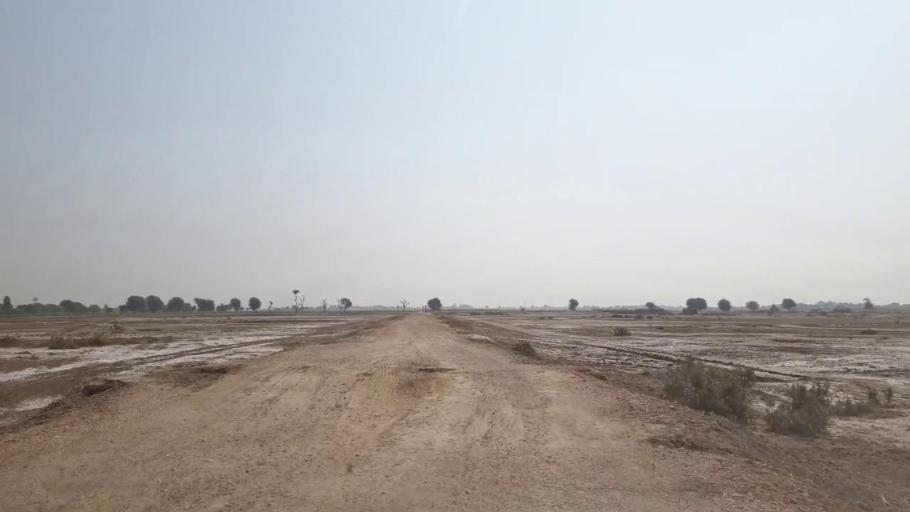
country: PK
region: Sindh
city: Mirpur Khas
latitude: 25.6485
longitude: 69.1370
